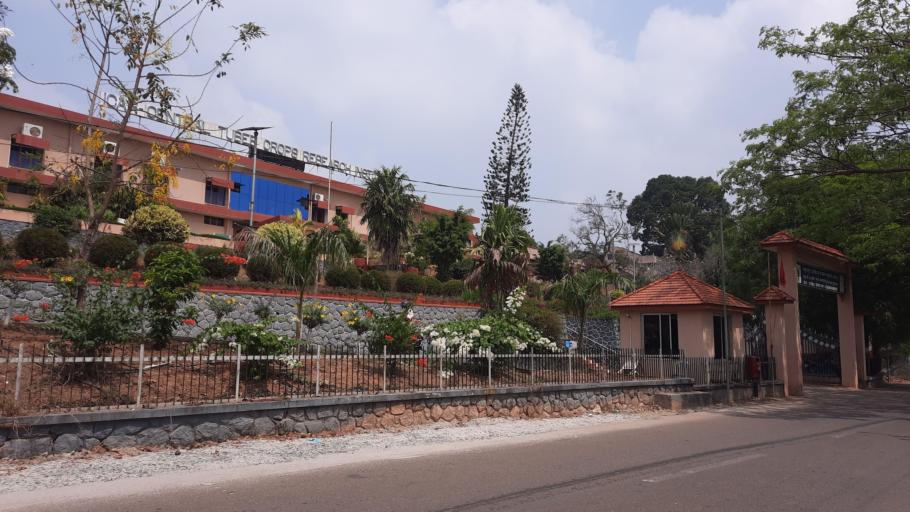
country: IN
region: Kerala
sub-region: Thiruvananthapuram
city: Thiruvananthapuram
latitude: 8.5449
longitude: 76.9151
